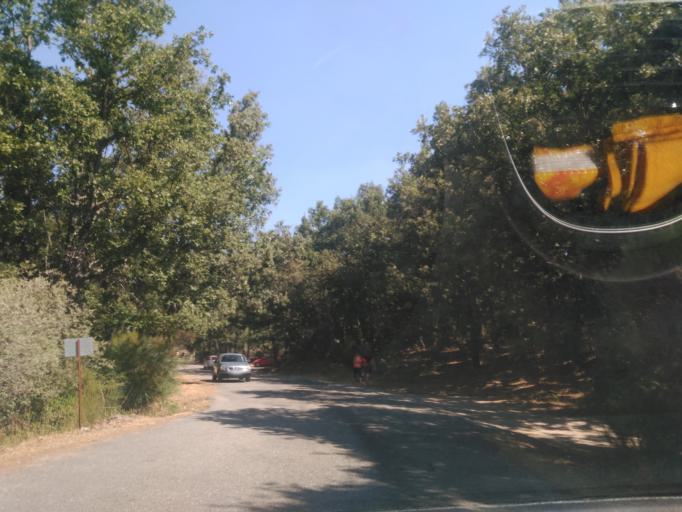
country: ES
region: Castille and Leon
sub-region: Provincia de Zamora
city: Galende
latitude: 42.1205
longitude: -6.6978
